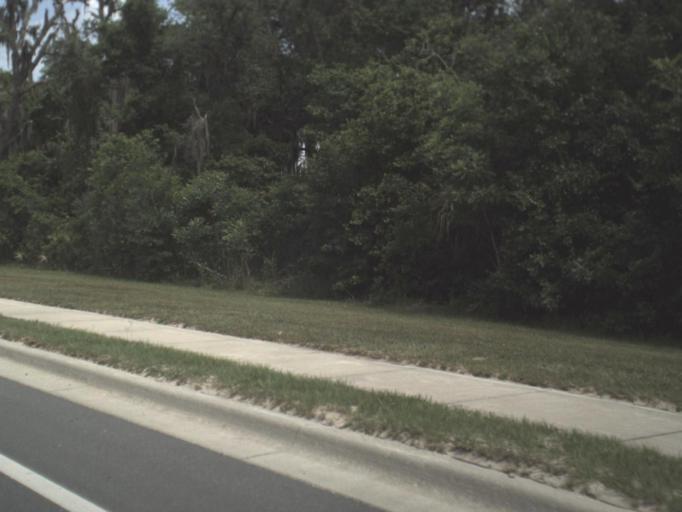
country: US
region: Florida
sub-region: Putnam County
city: Interlachen
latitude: 29.6261
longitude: -81.8563
